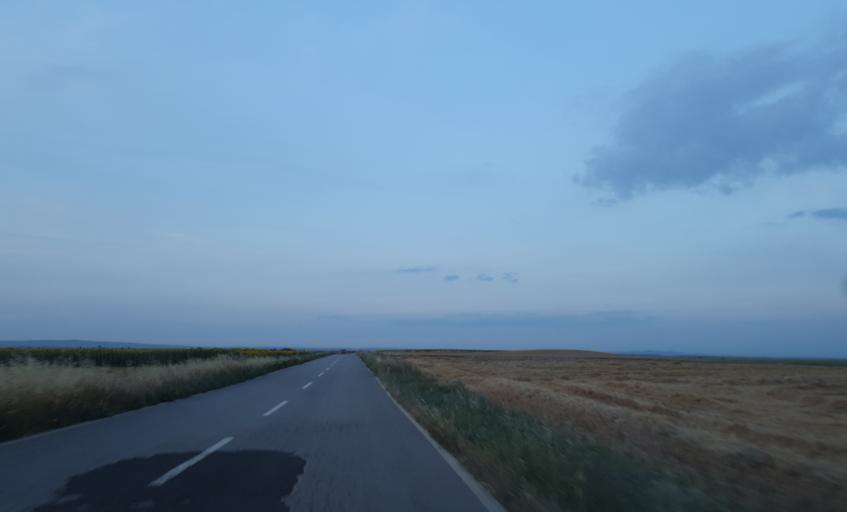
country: TR
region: Tekirdag
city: Beyazkoy
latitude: 41.4215
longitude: 27.6703
